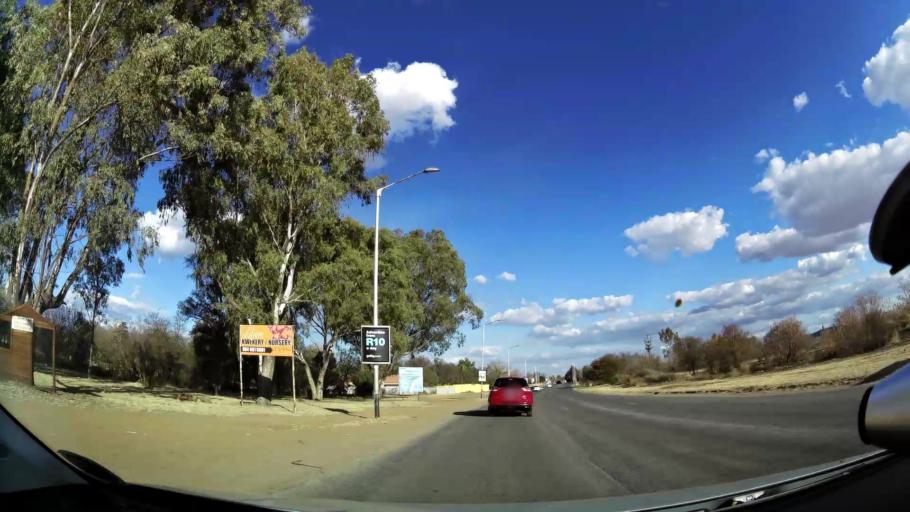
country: ZA
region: North-West
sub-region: Dr Kenneth Kaunda District Municipality
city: Klerksdorp
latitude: -26.8475
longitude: 26.6633
